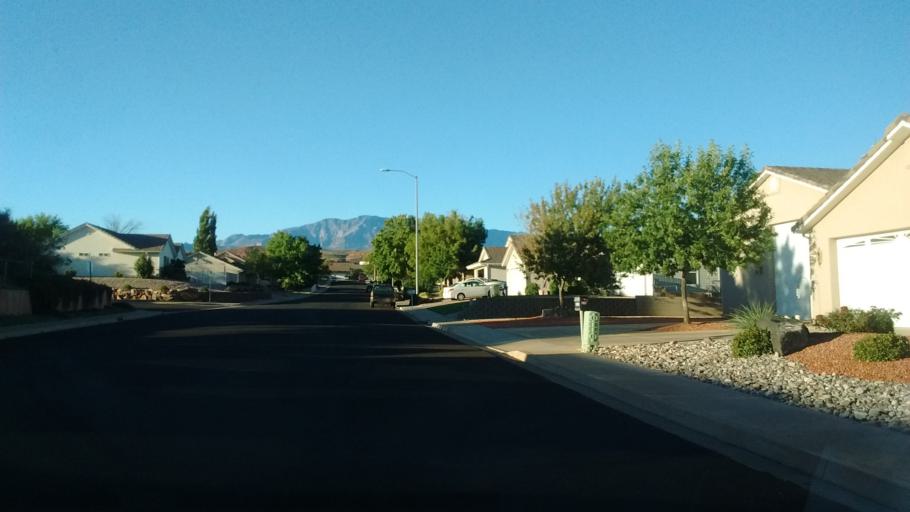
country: US
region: Utah
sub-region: Washington County
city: Washington
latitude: 37.1372
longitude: -113.4961
